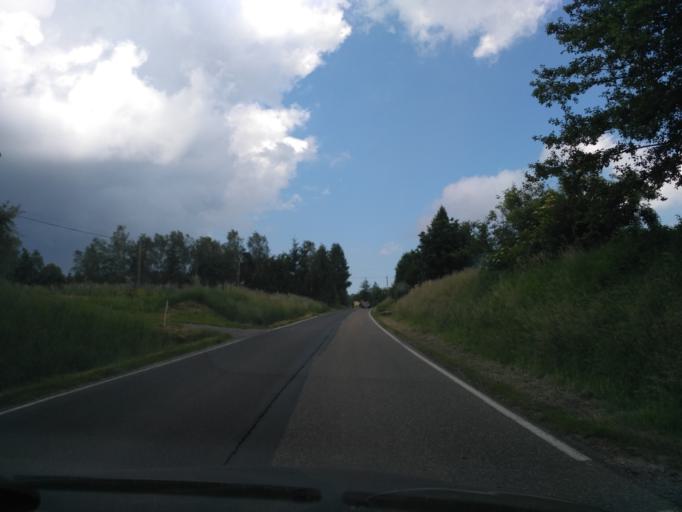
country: PL
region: Subcarpathian Voivodeship
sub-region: Powiat rzeszowski
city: Hyzne
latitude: 49.9580
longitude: 22.1990
